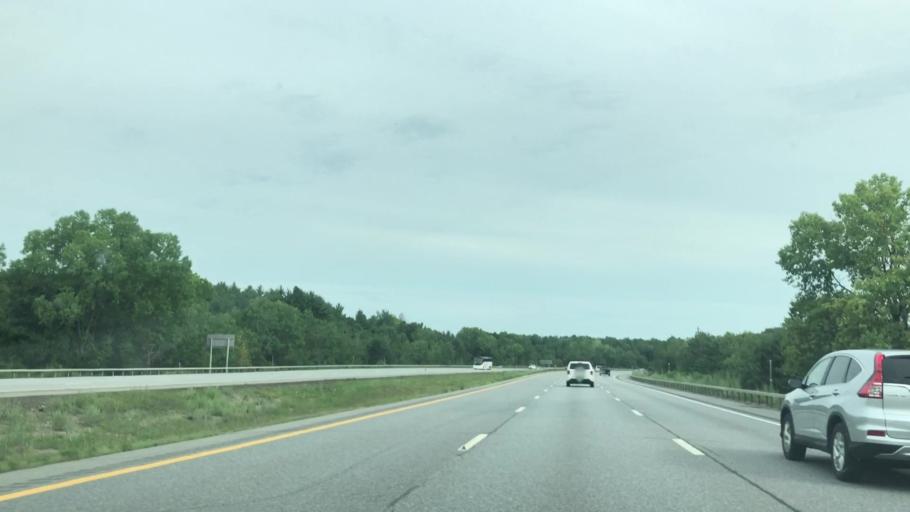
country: US
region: New York
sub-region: Warren County
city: Glens Falls North
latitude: 43.3198
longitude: -73.6775
